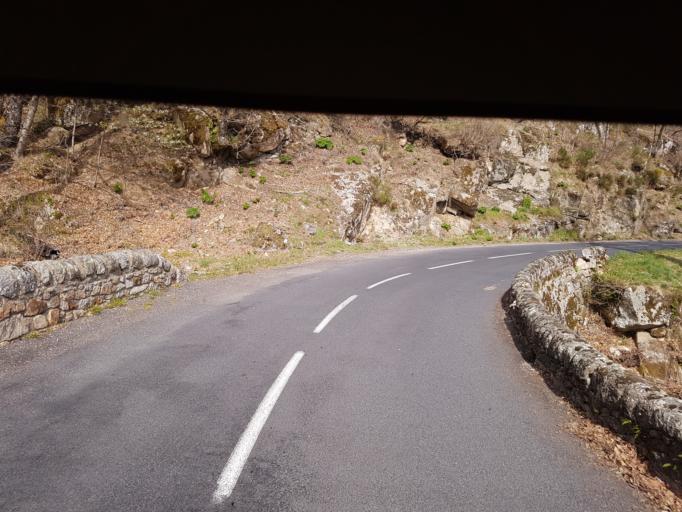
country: FR
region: Languedoc-Roussillon
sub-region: Departement de la Lozere
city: Florac
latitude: 44.3622
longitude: 3.7263
